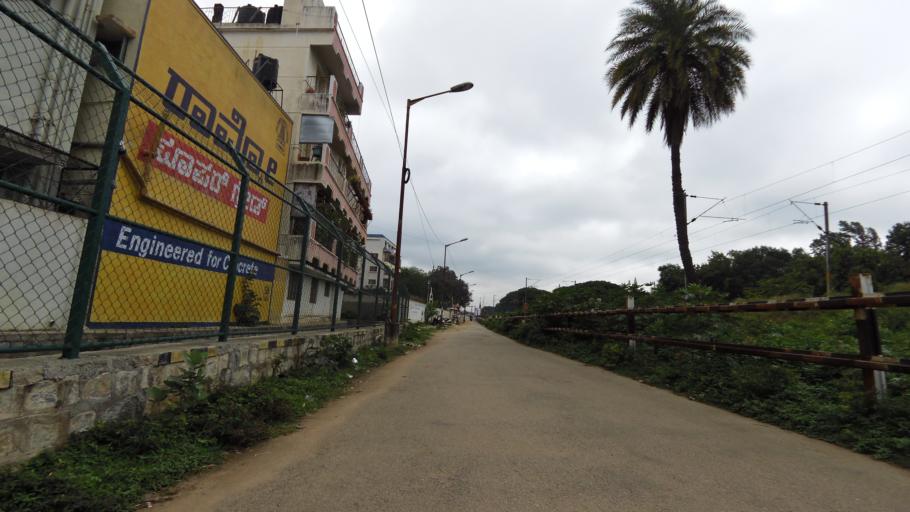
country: IN
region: Karnataka
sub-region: Bangalore Urban
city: Bangalore
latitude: 12.9945
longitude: 77.6301
